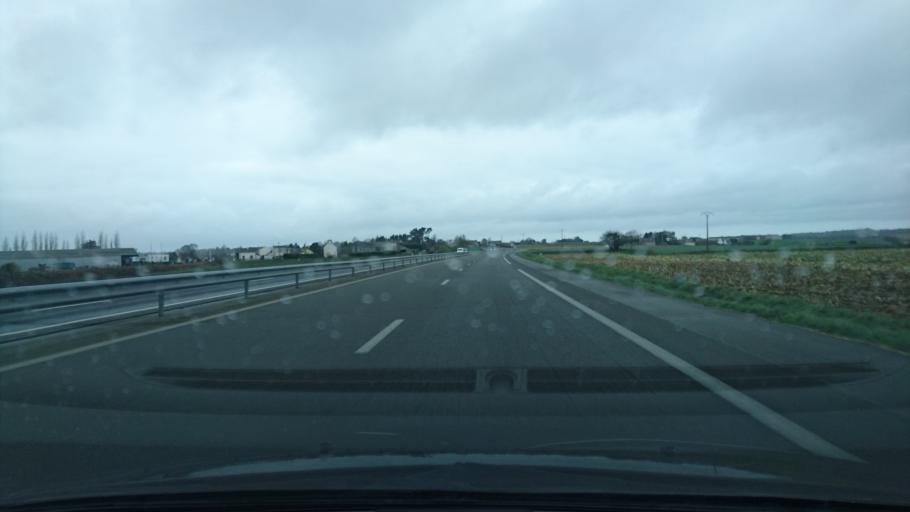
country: FR
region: Brittany
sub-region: Departement du Finistere
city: Taule
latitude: 48.6124
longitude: -3.8920
